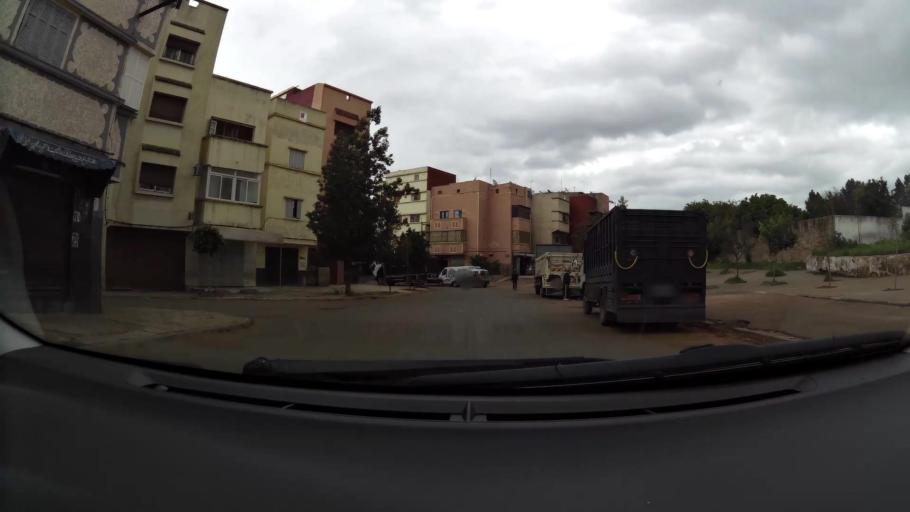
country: MA
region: Grand Casablanca
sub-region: Casablanca
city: Casablanca
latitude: 33.5586
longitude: -7.5591
